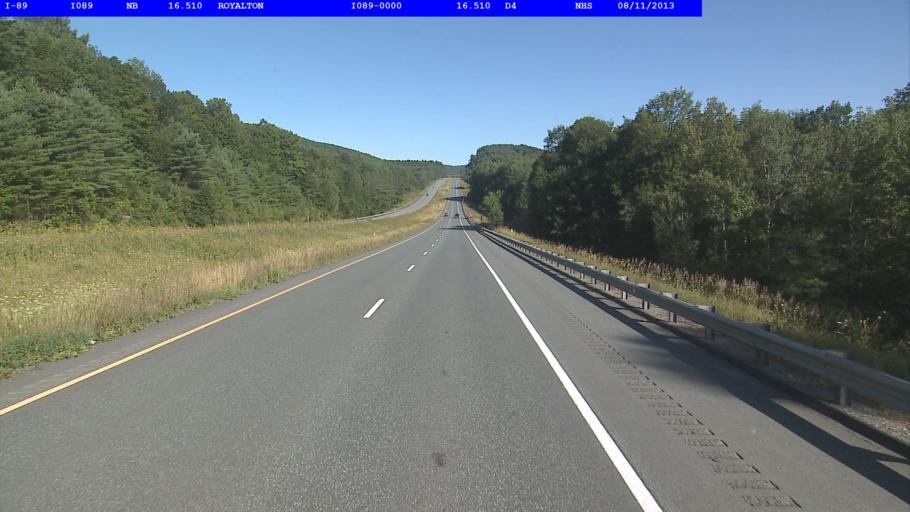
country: US
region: Vermont
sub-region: Windsor County
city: Woodstock
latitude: 43.7958
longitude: -72.5066
